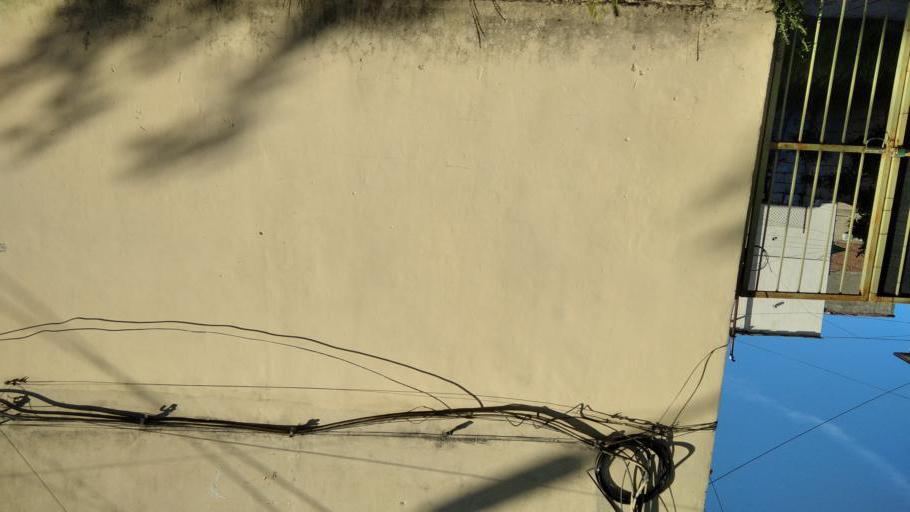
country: AL
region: Shkoder
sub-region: Rrethi i Shkodres
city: Shkoder
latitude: 42.0588
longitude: 19.5138
